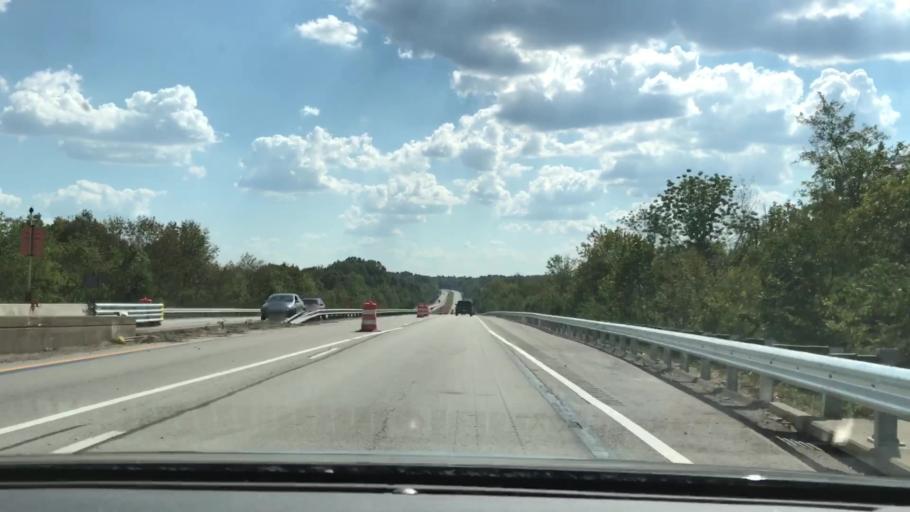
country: US
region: Kentucky
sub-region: Ohio County
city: Oak Grove
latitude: 37.2812
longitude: -86.7440
